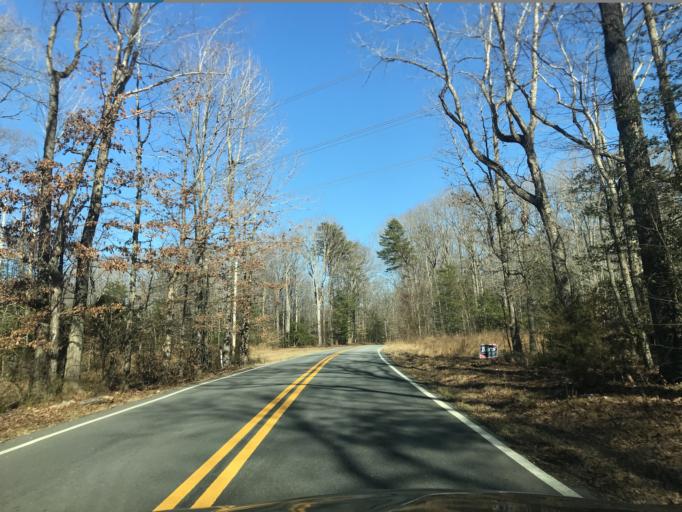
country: US
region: Virginia
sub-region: Prince William County
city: Cherry Hill
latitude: 38.5124
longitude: -77.2452
